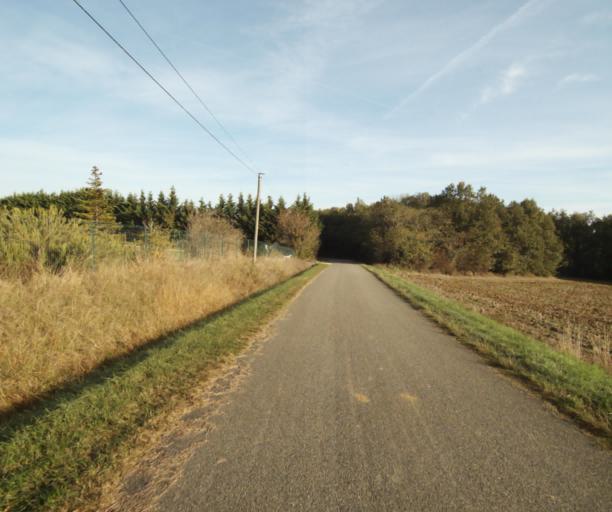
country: FR
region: Midi-Pyrenees
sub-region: Departement du Tarn-et-Garonne
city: Nohic
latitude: 43.9106
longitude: 1.4799
